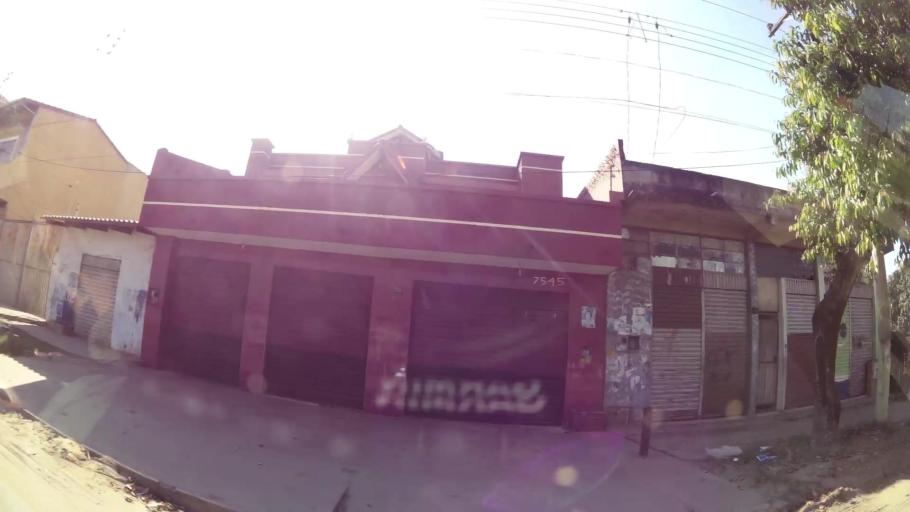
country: BO
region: Santa Cruz
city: Santa Cruz de la Sierra
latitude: -17.8219
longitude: -63.1257
